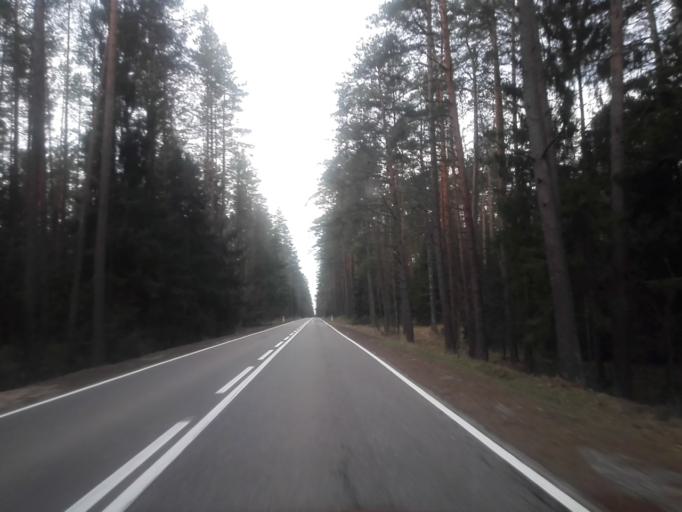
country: PL
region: Podlasie
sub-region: Powiat augustowski
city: Augustow
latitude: 53.8811
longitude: 23.1079
